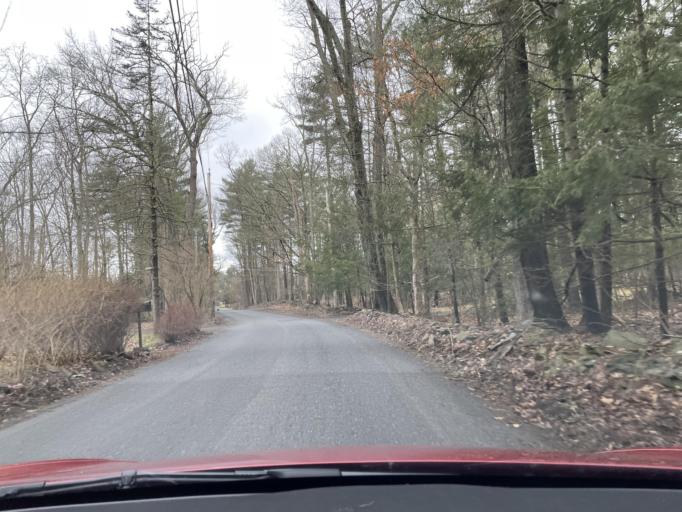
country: US
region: New York
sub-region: Ulster County
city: Manorville
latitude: 42.0911
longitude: -74.0365
